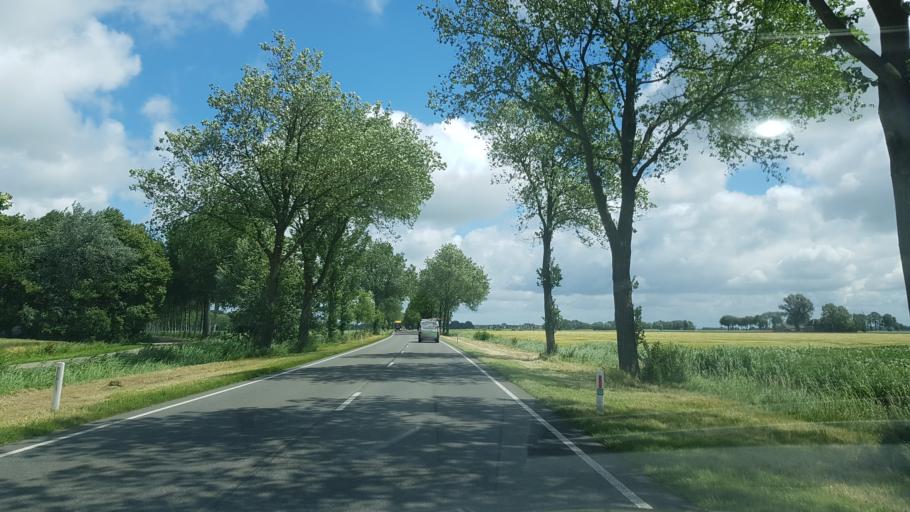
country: NL
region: Groningen
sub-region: Gemeente Bedum
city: Bedum
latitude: 53.4064
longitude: 6.6312
